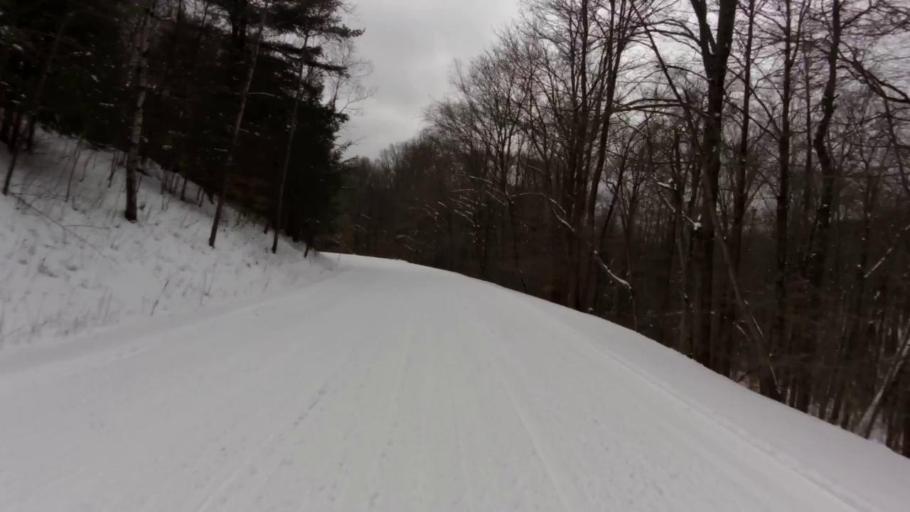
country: US
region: New York
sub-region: Cattaraugus County
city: Salamanca
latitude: 42.0388
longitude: -78.7864
